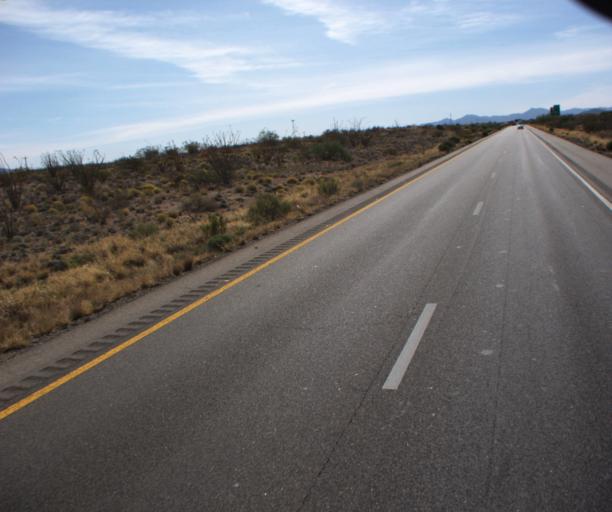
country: US
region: Arizona
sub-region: Pima County
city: Vail
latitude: 32.0200
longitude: -110.7101
